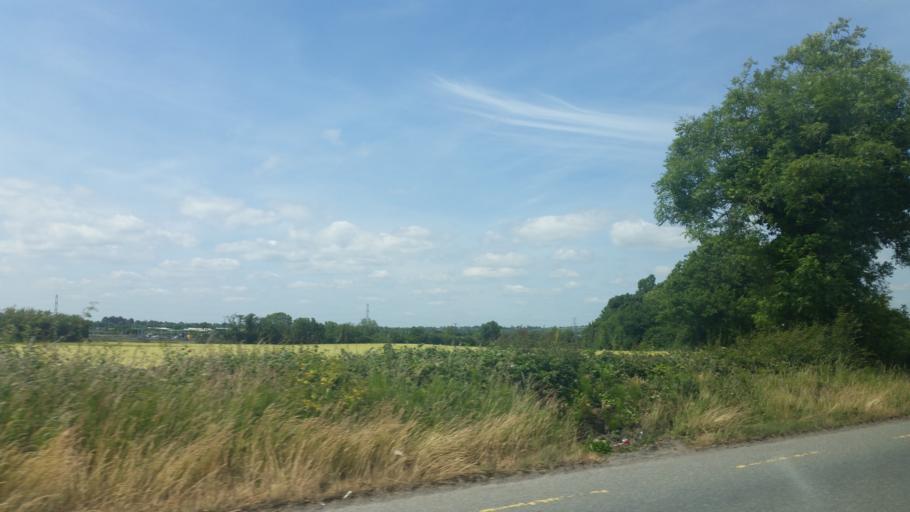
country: IE
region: Leinster
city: Lusk
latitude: 53.5410
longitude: -6.2018
